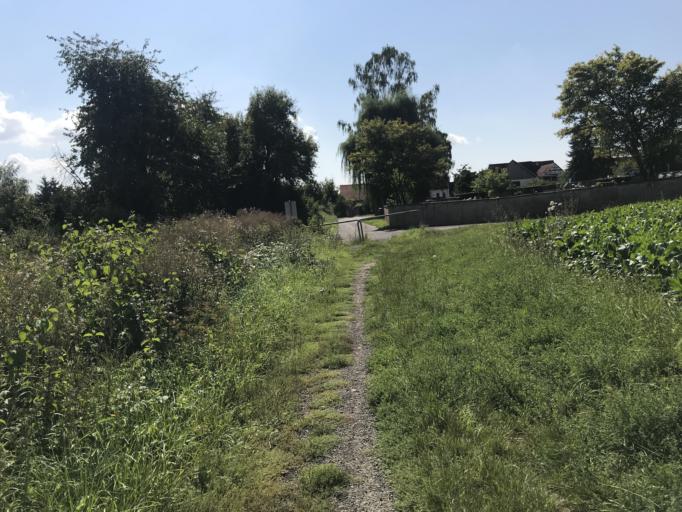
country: DE
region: Hesse
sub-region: Regierungsbezirk Giessen
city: Hungen
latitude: 50.4378
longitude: 8.8902
